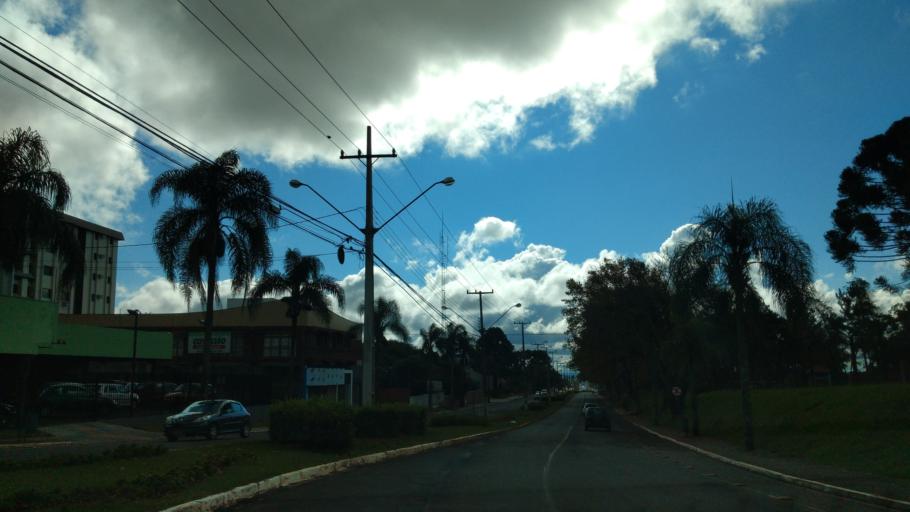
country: BR
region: Parana
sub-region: Guarapuava
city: Guarapuava
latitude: -25.3858
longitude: -51.4645
